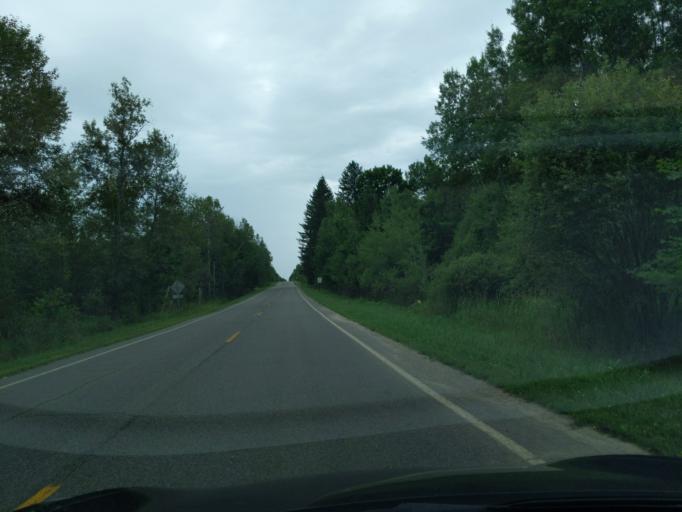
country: US
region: Michigan
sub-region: Clare County
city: Harrison
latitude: 44.0157
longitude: -84.9493
